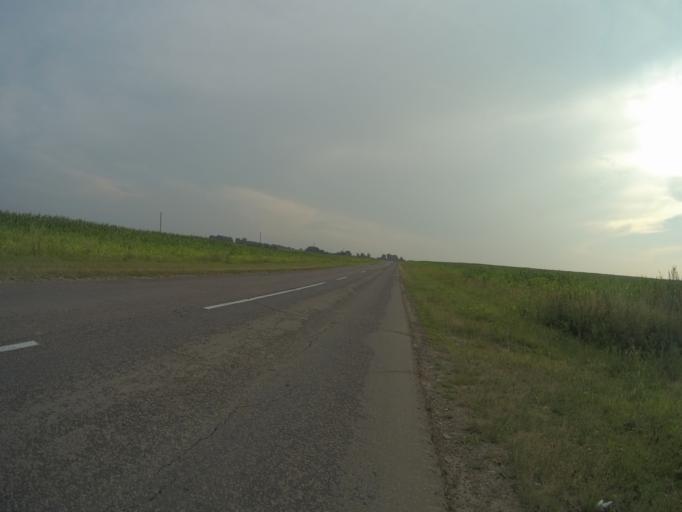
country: RU
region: Ivanovo
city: Gavrilov Posad
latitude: 56.3511
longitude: 40.2140
